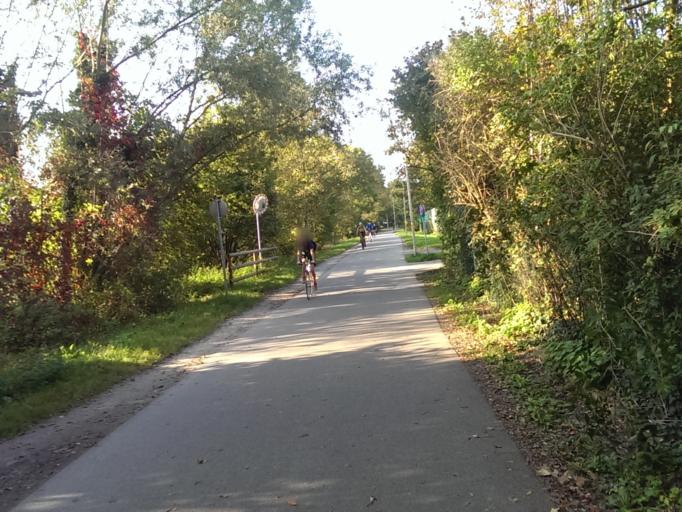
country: AT
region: Styria
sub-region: Graz Stadt
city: Goesting
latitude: 47.0881
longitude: 15.4238
